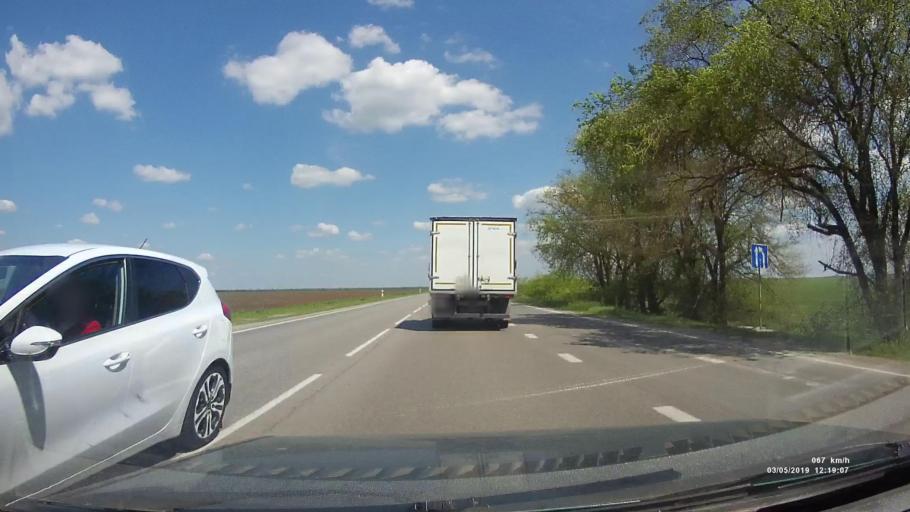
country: RU
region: Rostov
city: Melikhovskaya
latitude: 47.3982
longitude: 40.6045
